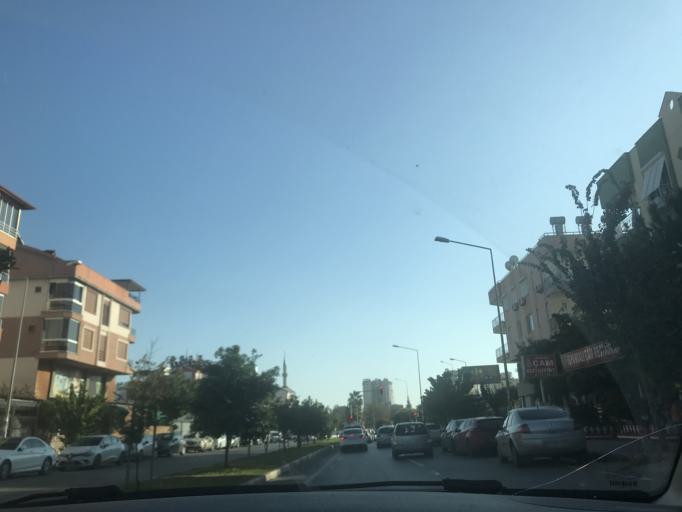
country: TR
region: Antalya
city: Antalya
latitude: 36.8846
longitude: 30.6480
